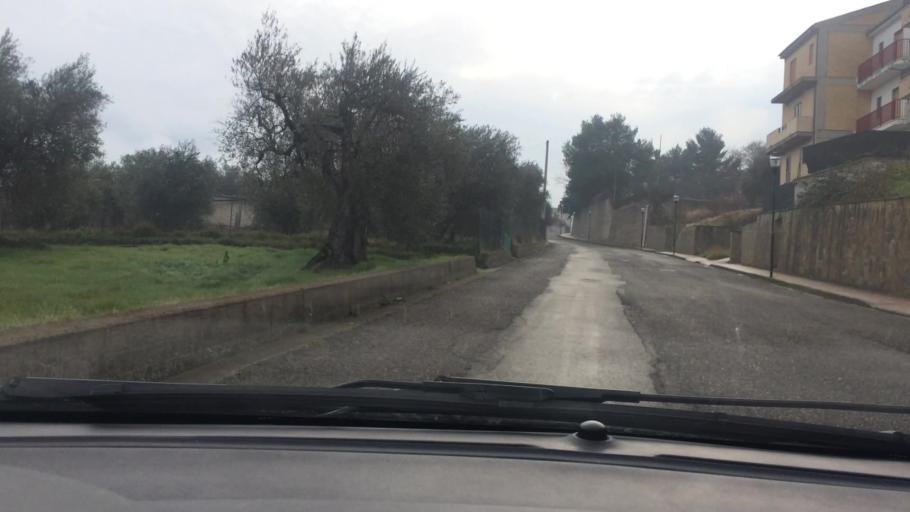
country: IT
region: Basilicate
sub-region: Provincia di Matera
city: San Mauro Forte
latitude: 40.4888
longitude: 16.2445
